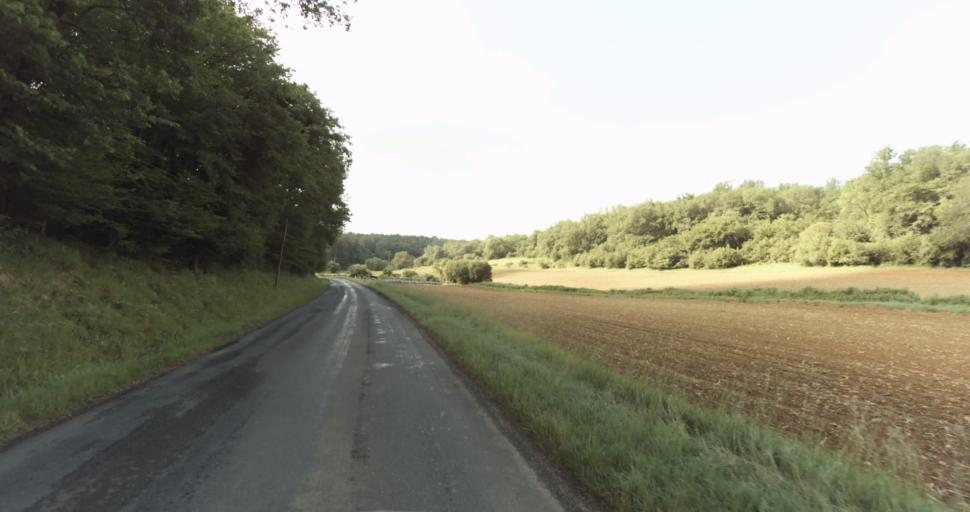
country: FR
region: Aquitaine
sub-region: Departement de la Dordogne
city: Lalinde
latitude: 44.8821
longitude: 0.7763
